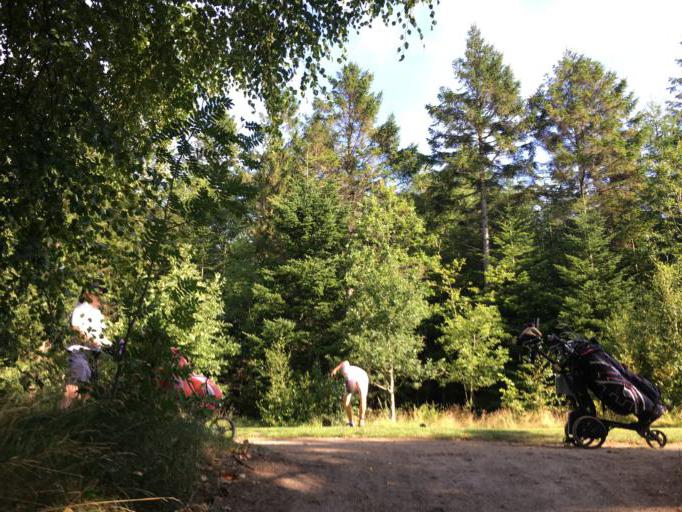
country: DK
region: Central Jutland
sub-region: Holstebro Kommune
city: Ulfborg
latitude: 56.3301
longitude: 8.4156
